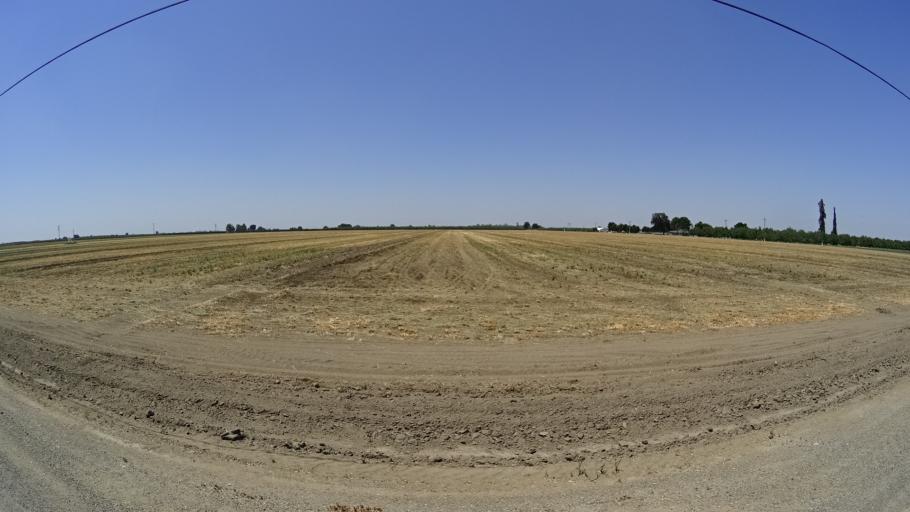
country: US
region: California
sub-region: Kings County
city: Armona
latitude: 36.3705
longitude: -119.7270
